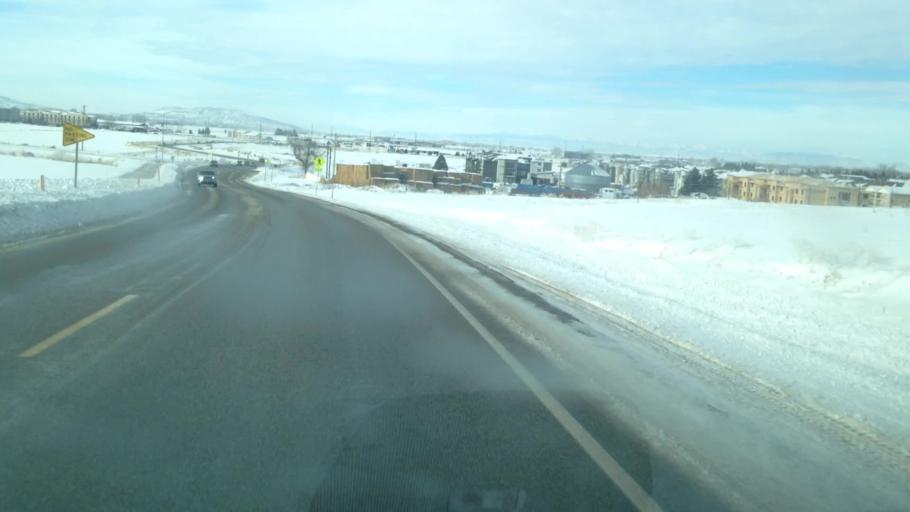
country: US
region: Idaho
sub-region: Madison County
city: Rexburg
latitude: 43.8045
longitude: -111.7951
